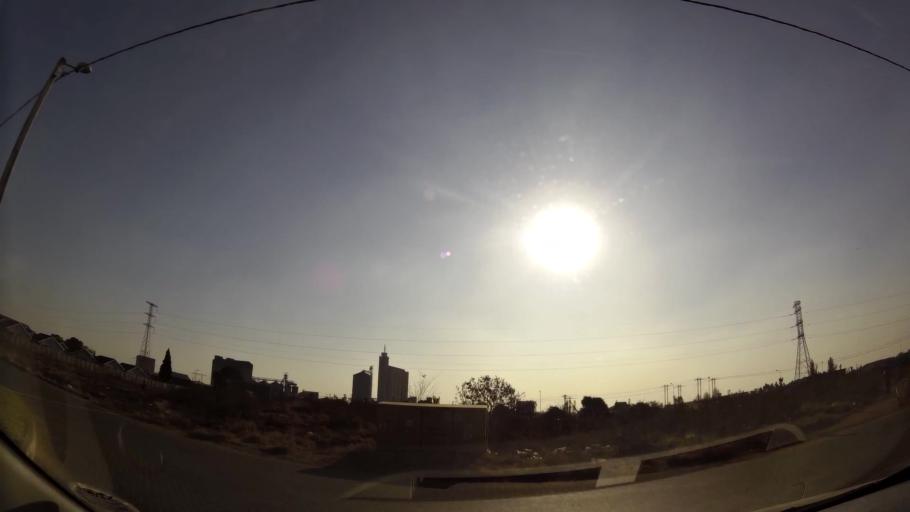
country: ZA
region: Gauteng
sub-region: West Rand District Municipality
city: Randfontein
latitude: -26.1884
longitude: 27.6972
